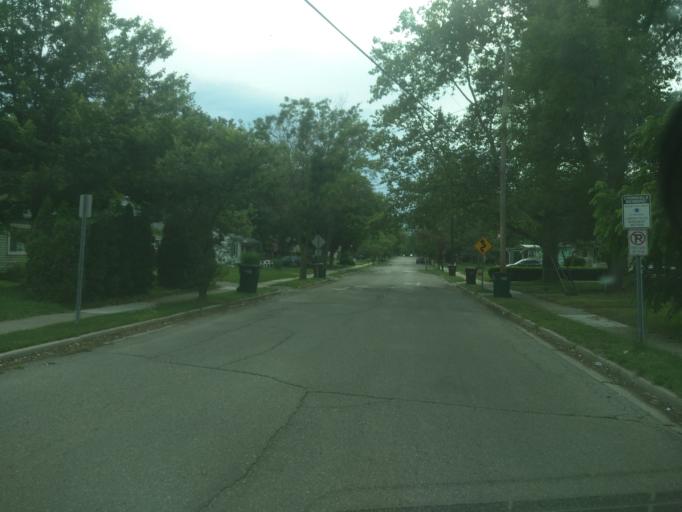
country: US
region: Michigan
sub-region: Ingham County
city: Lansing
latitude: 42.6912
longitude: -84.5776
